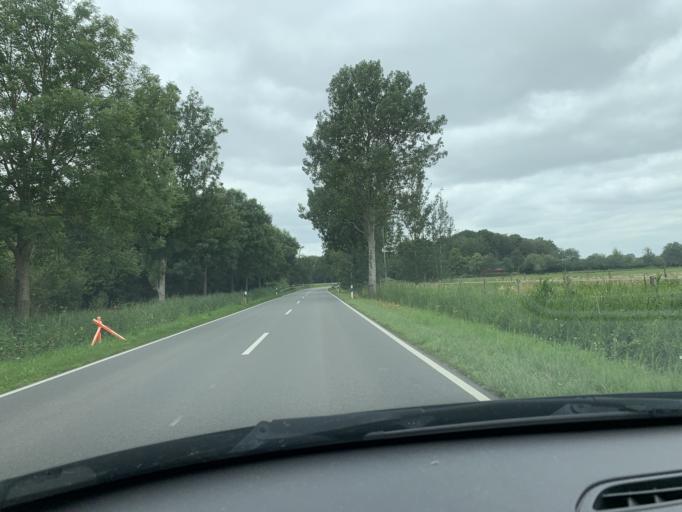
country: DE
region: Lower Saxony
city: Wiefelstede
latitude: 53.2116
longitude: 8.0722
